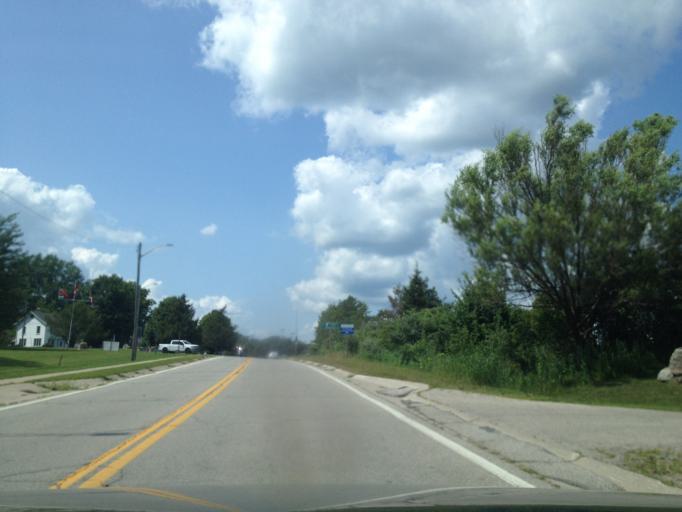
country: CA
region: Ontario
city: Aylmer
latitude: 42.6512
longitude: -80.8091
